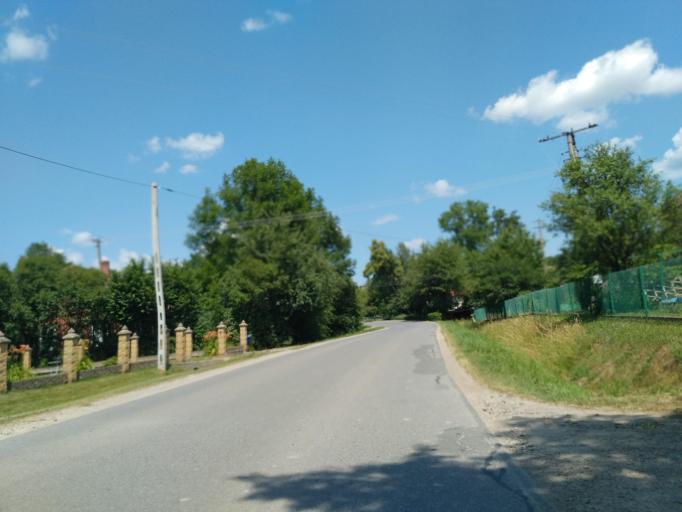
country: PL
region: Subcarpathian Voivodeship
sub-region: Powiat sanocki
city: Niebieszczany
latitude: 49.4969
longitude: 22.1661
